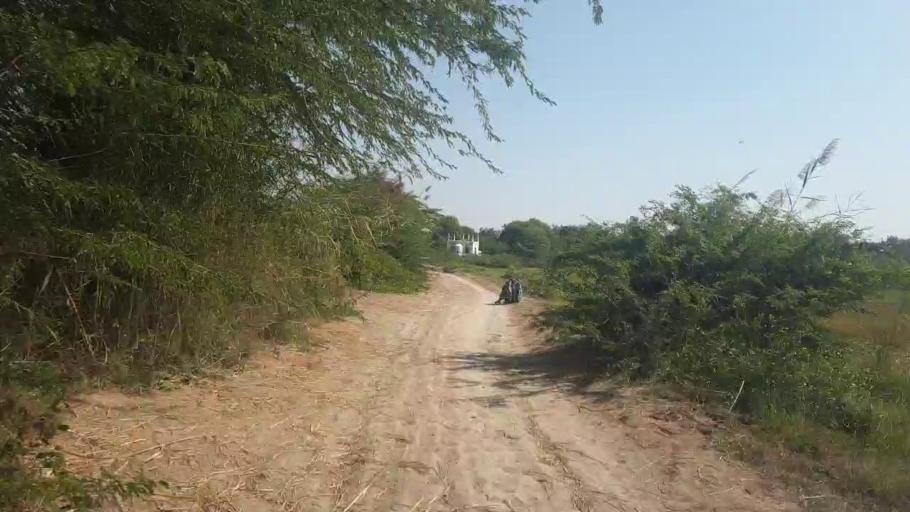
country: PK
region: Sindh
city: Badin
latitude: 24.6832
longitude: 68.8766
